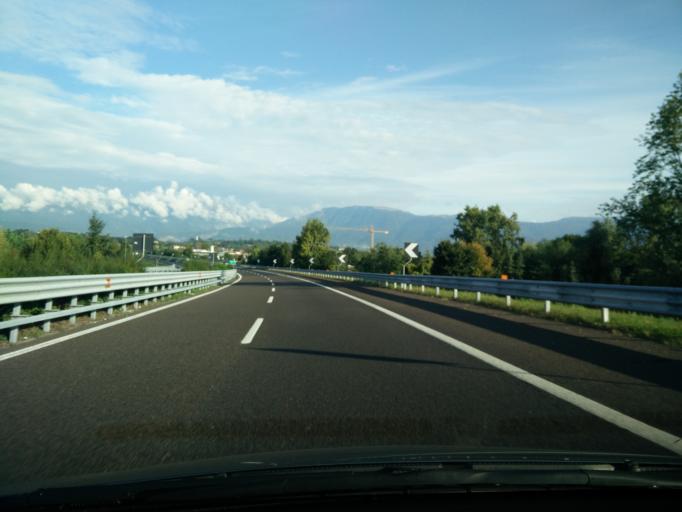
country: IT
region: Veneto
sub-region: Provincia di Treviso
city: San Martino
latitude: 45.9033
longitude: 12.3452
